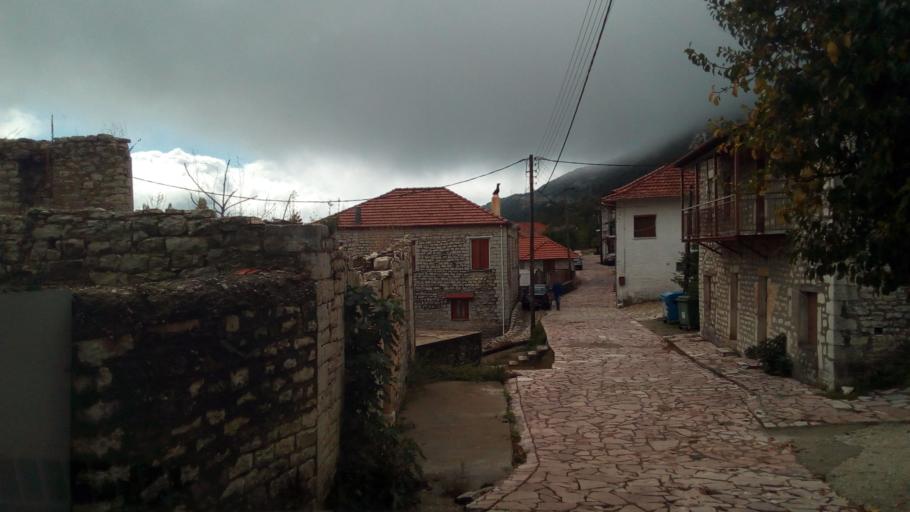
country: GR
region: West Greece
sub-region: Nomos Aitolias kai Akarnanias
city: Thermo
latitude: 38.5985
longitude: 21.7933
